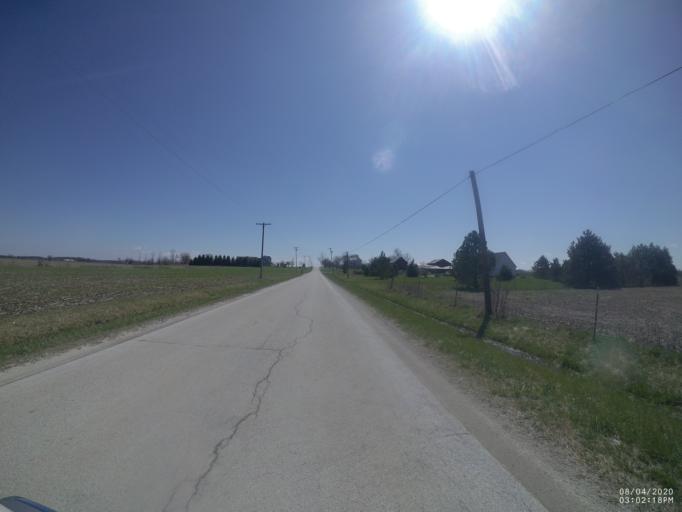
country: US
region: Ohio
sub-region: Sandusky County
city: Stony Prairie
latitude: 41.3400
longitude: -83.2393
